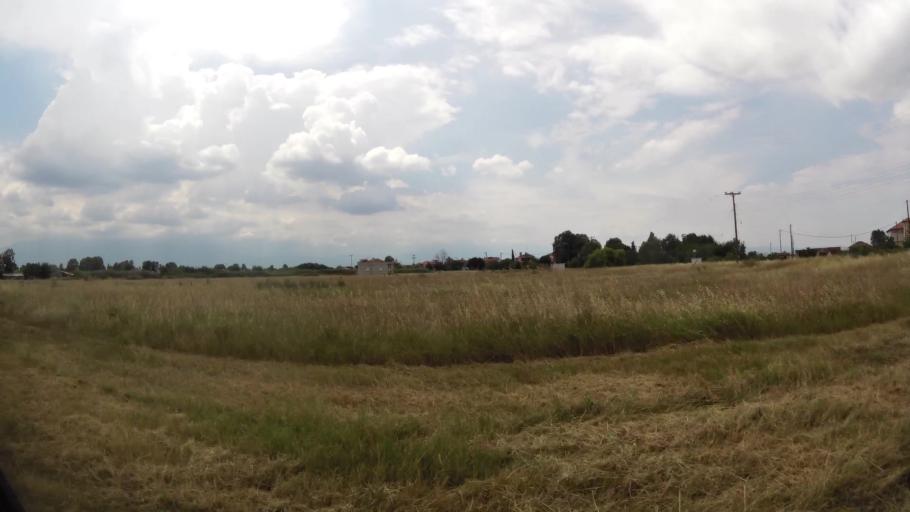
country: GR
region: Central Macedonia
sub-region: Nomos Pierias
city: Paralia
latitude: 40.2756
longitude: 22.5920
